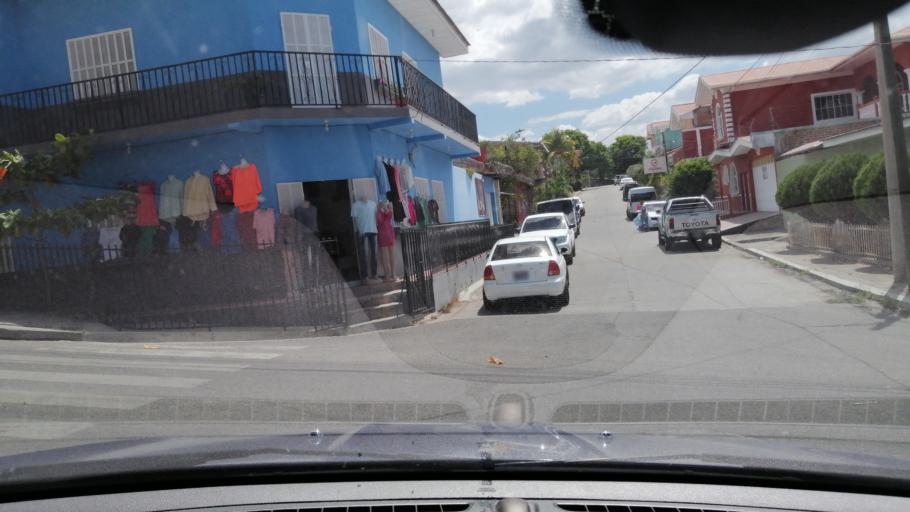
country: SV
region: Santa Ana
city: Metapan
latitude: 14.3342
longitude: -89.4412
